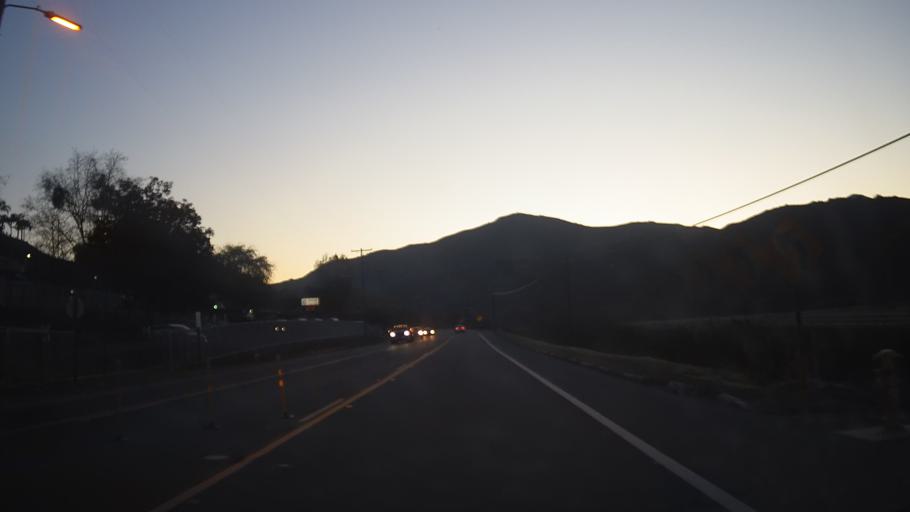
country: US
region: California
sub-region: San Diego County
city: Crest
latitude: 32.7812
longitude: -116.8514
